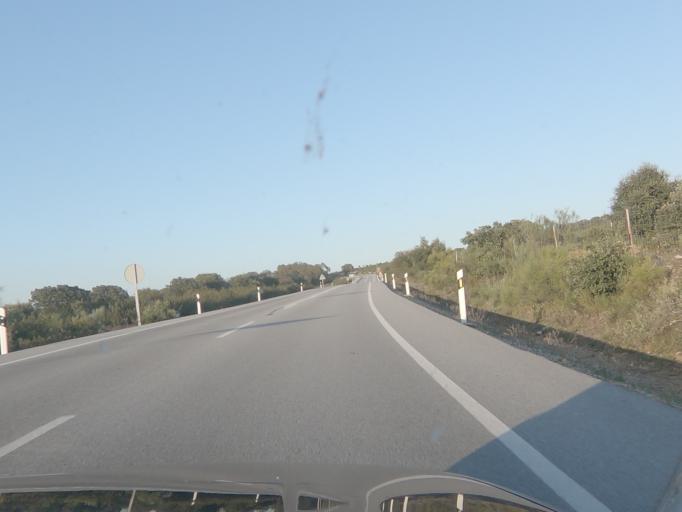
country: ES
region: Extremadura
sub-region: Provincia de Caceres
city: Valencia de Alcantara
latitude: 39.4906
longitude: -7.2005
